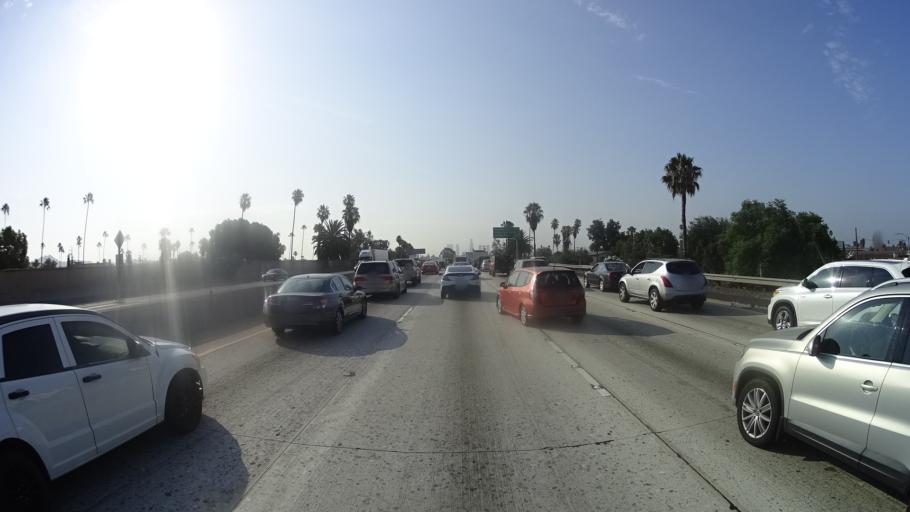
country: US
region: California
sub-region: Los Angeles County
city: Hollywood
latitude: 34.0856
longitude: -118.3018
